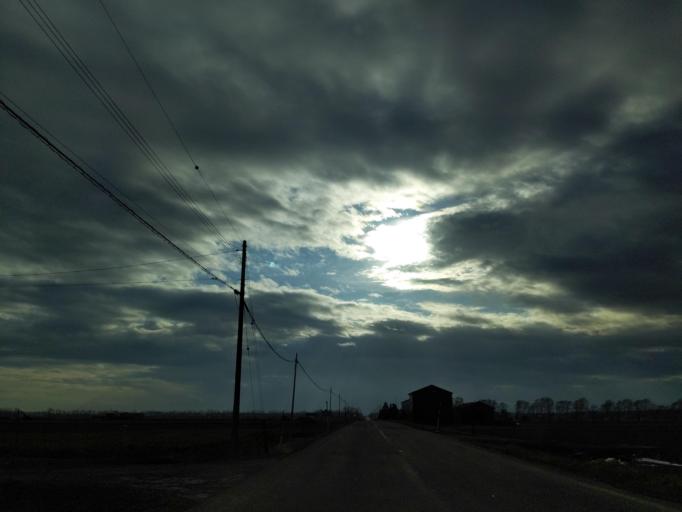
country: JP
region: Hokkaido
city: Kitahiroshima
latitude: 42.9880
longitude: 141.6544
